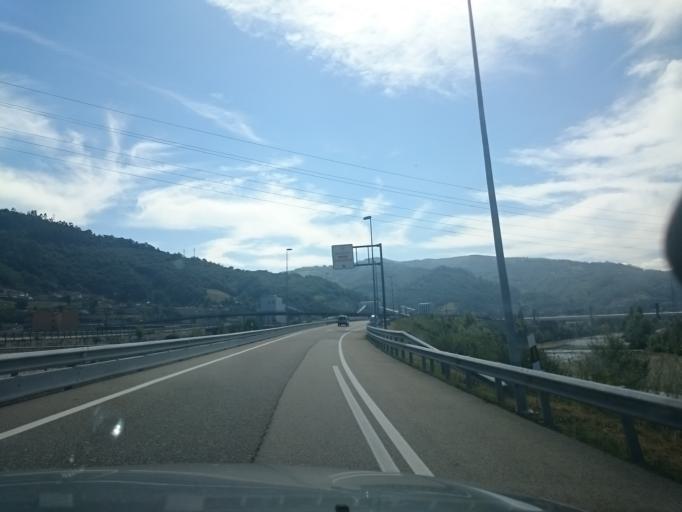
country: ES
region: Asturias
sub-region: Province of Asturias
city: Mieres
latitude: 43.2632
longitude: -5.7864
